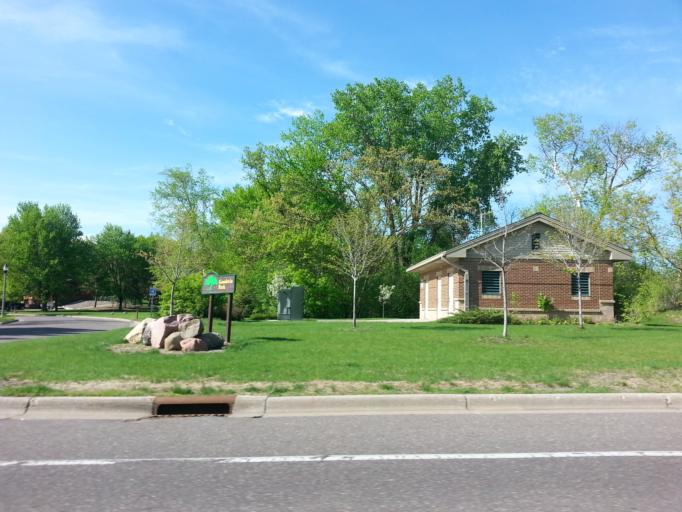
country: US
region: Minnesota
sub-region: Ramsey County
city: North Saint Paul
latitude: 45.0066
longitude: -92.9766
